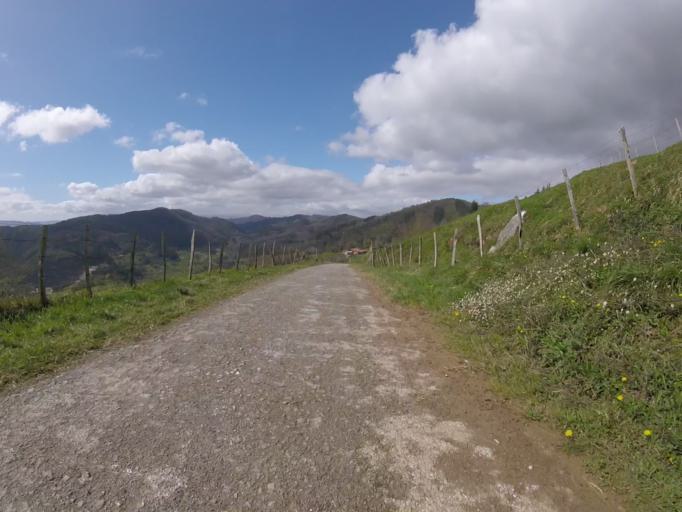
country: ES
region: Basque Country
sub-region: Provincia de Guipuzcoa
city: Albiztur
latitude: 43.1409
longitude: -2.1227
